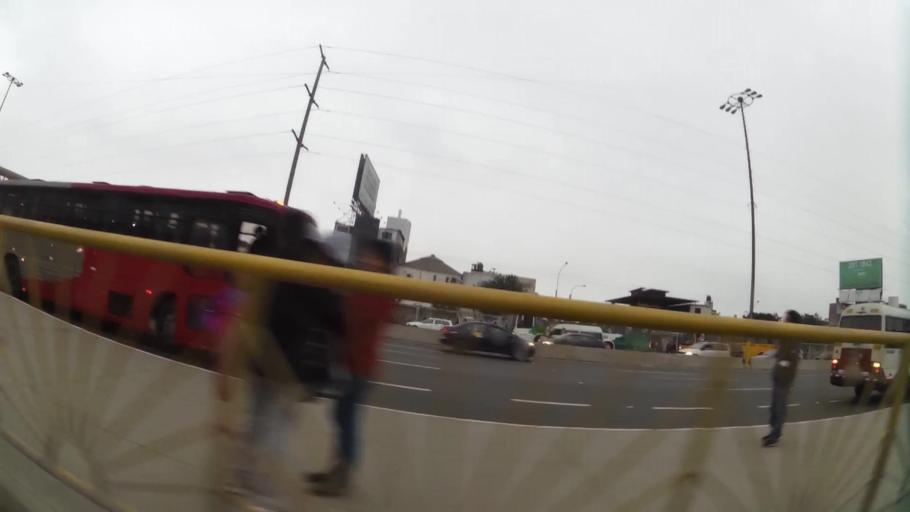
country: PE
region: Lima
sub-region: Lima
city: Surco
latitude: -12.1454
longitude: -76.9817
